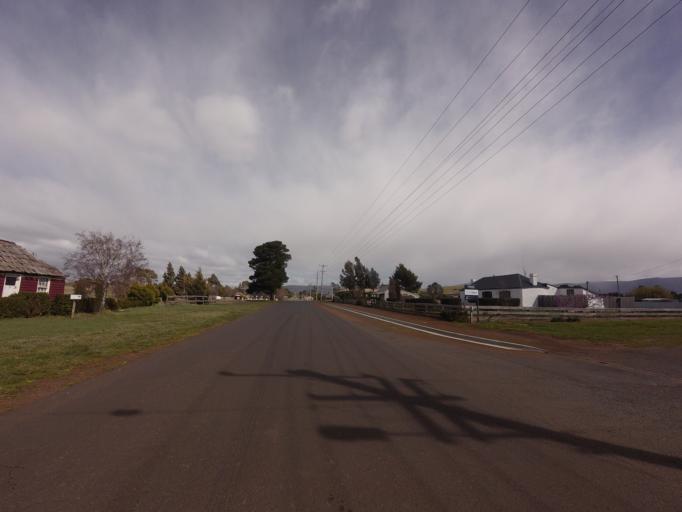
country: AU
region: Tasmania
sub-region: Northern Midlands
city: Evandale
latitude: -42.1419
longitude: 147.4223
